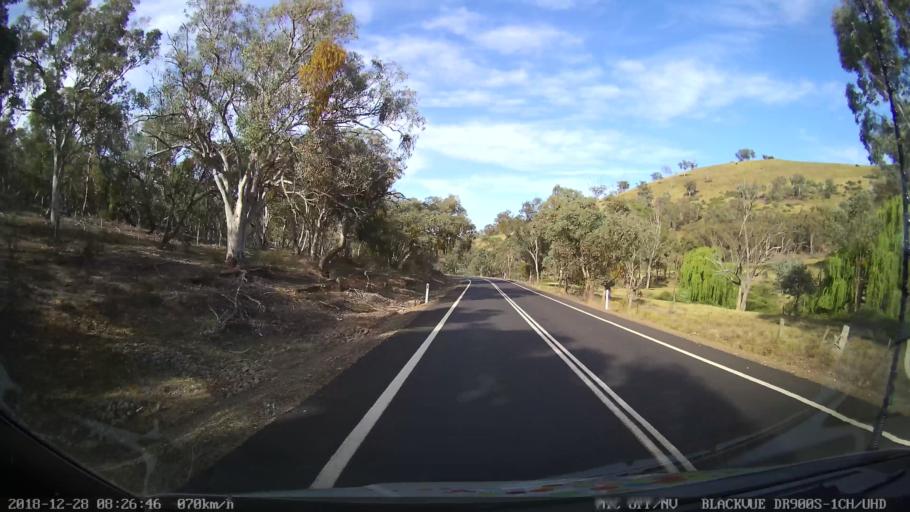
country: AU
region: New South Wales
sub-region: Blayney
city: Blayney
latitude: -33.9385
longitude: 149.3439
